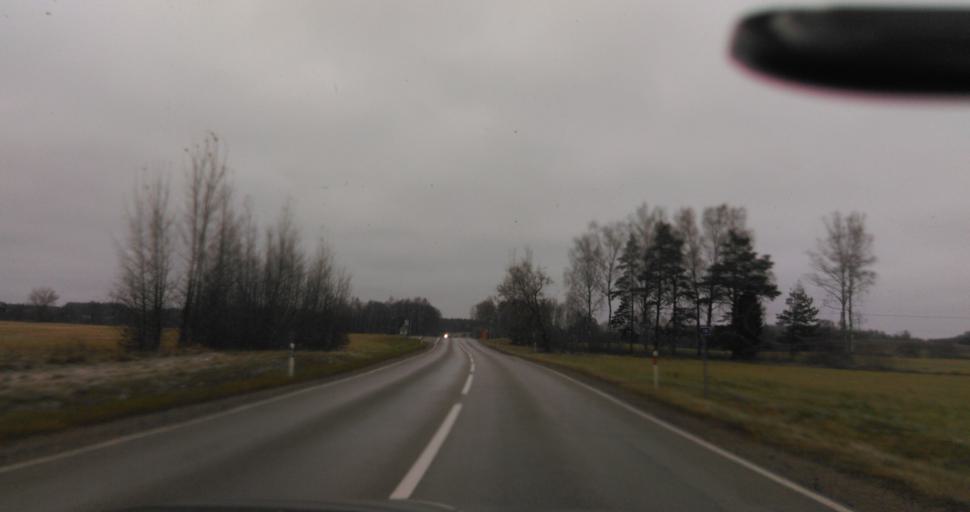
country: LT
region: Panevezys
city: Rokiskis
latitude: 55.8721
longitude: 25.5458
